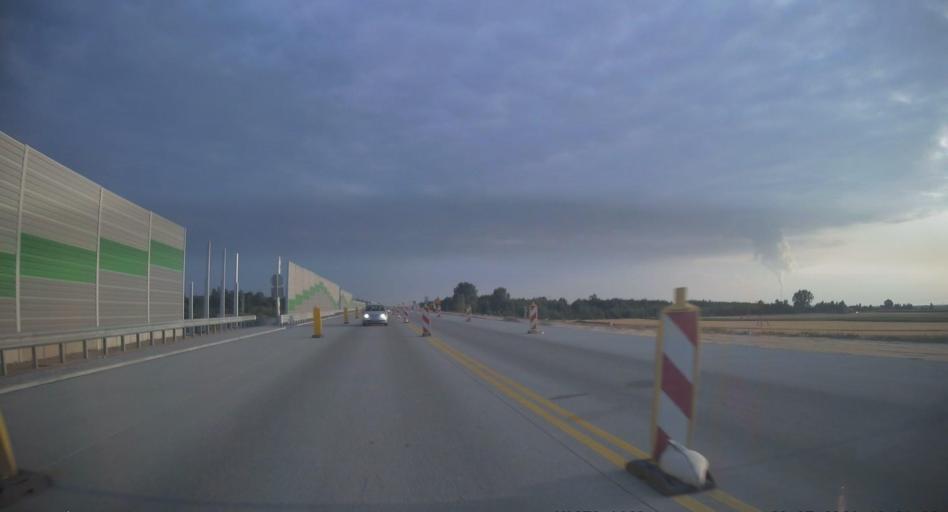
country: PL
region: Lodz Voivodeship
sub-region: Powiat piotrkowski
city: Wola Krzysztoporska
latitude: 51.3567
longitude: 19.6083
